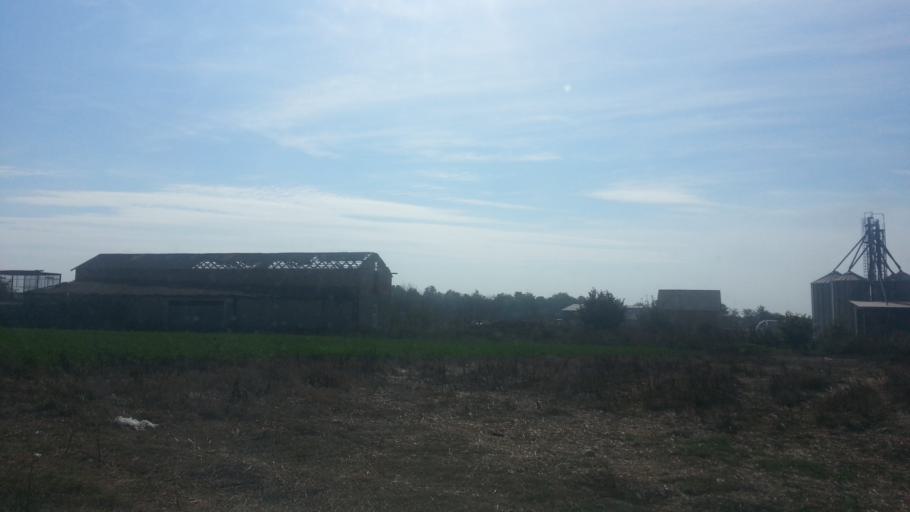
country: RS
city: Stari Banovci
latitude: 44.9986
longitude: 20.2783
